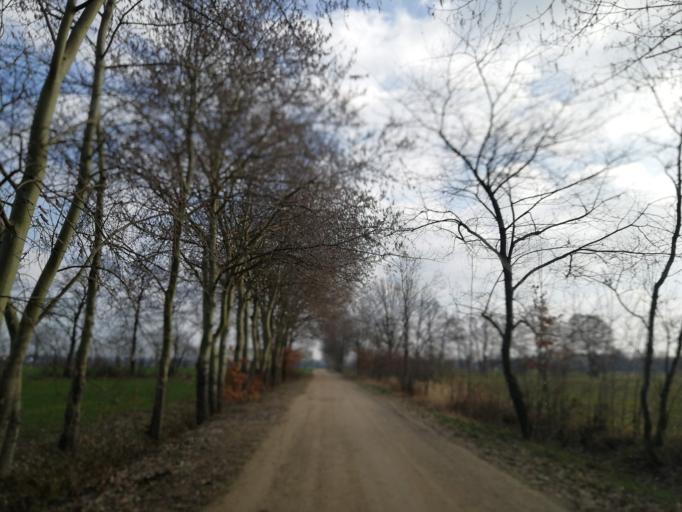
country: DE
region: Brandenburg
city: Finsterwalde
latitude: 51.6587
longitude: 13.7218
